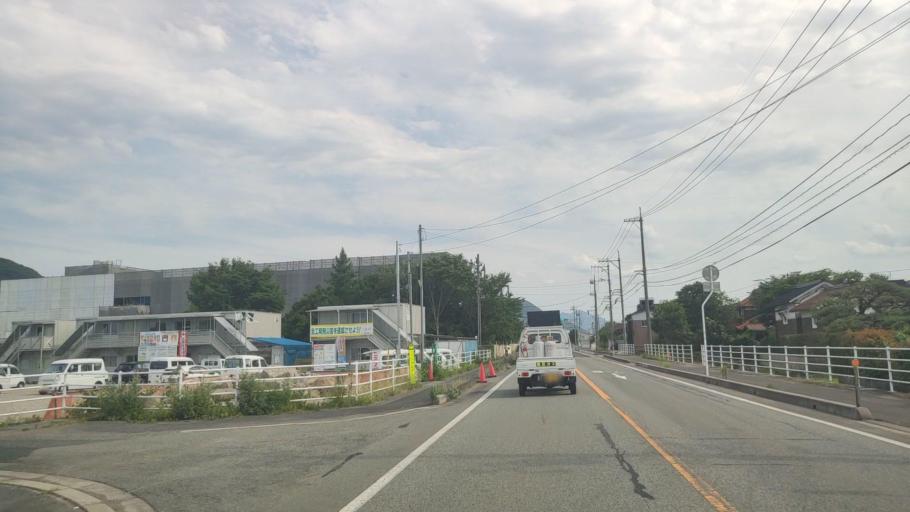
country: JP
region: Tottori
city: Tottori
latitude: 35.4550
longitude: 134.2032
